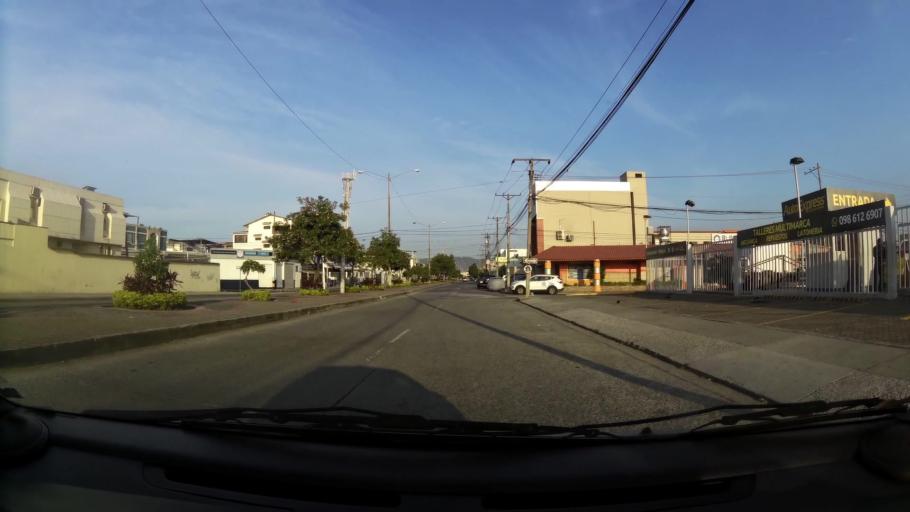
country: EC
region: Guayas
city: Eloy Alfaro
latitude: -2.1503
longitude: -79.8871
